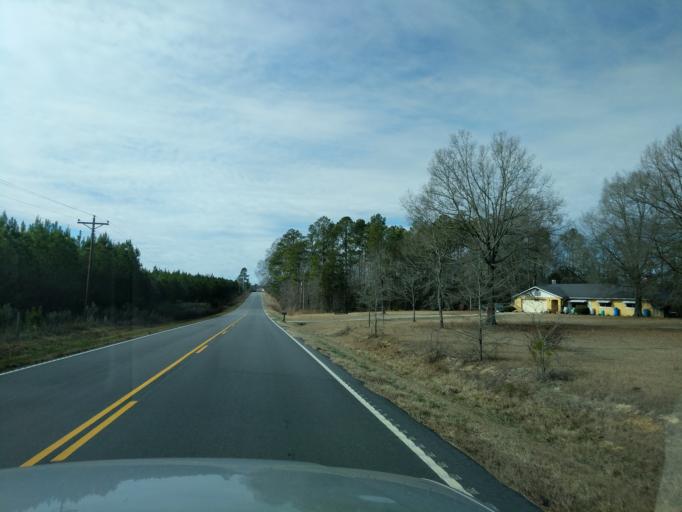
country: US
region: South Carolina
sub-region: Edgefield County
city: Edgefield
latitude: 33.9357
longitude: -81.9611
